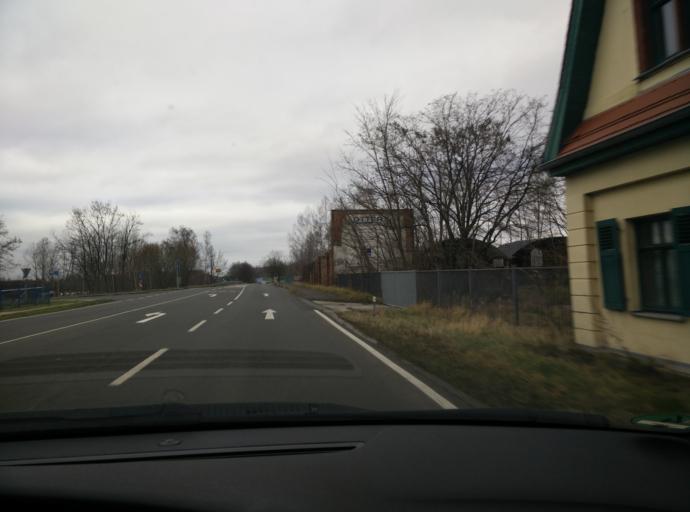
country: DE
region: Saxony
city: Frohburg
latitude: 51.0916
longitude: 12.5281
